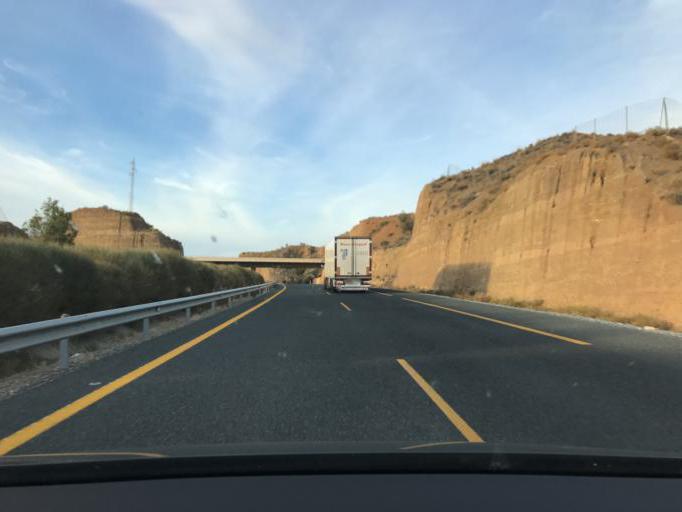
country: ES
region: Andalusia
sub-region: Provincia de Granada
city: Guadix
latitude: 37.3147
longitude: -3.1121
